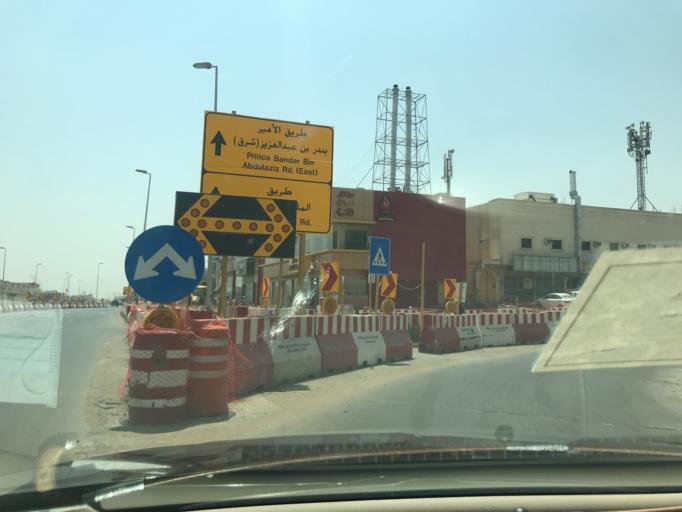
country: SA
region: Ar Riyad
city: Riyadh
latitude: 24.7482
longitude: 46.7736
